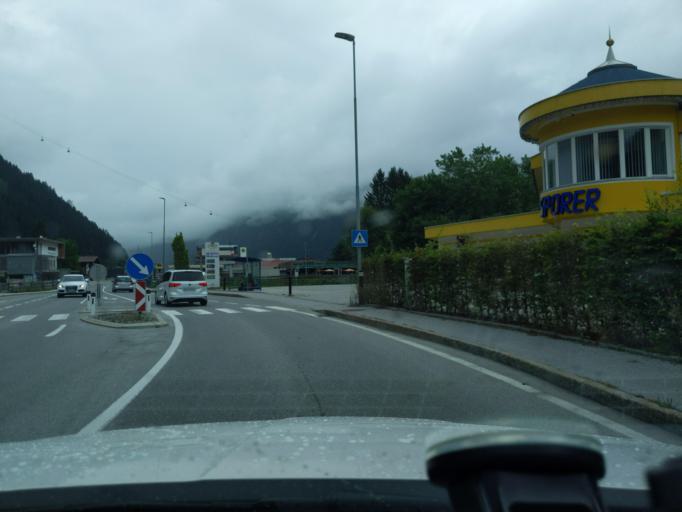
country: AT
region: Tyrol
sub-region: Politischer Bezirk Schwaz
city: Mayrhofen
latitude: 47.1586
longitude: 11.8474
